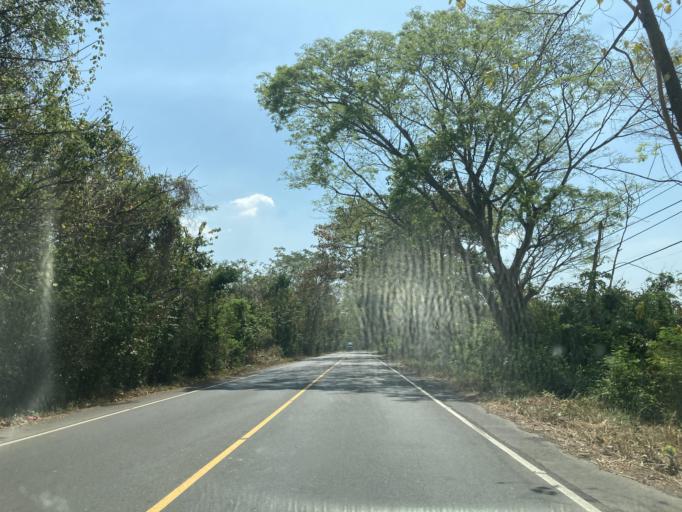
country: GT
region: Escuintla
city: Guanagazapa
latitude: 14.1818
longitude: -90.6899
